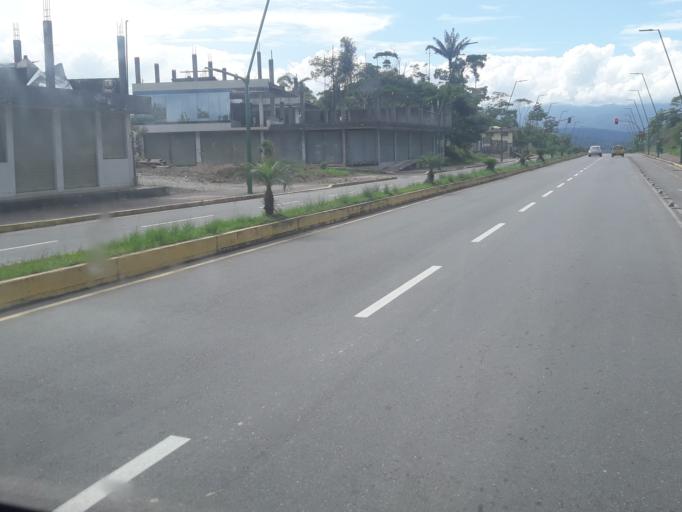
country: EC
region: Napo
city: Tena
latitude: -1.0176
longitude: -77.8070
